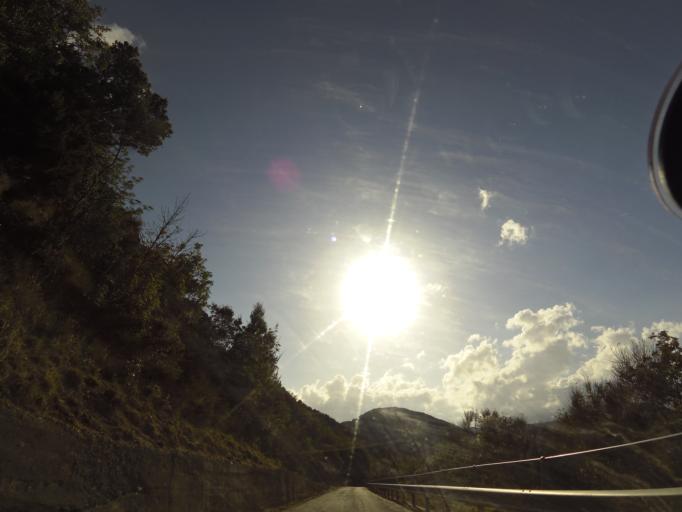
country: IT
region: Calabria
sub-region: Provincia di Reggio Calabria
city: Pazzano
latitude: 38.4655
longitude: 16.4358
